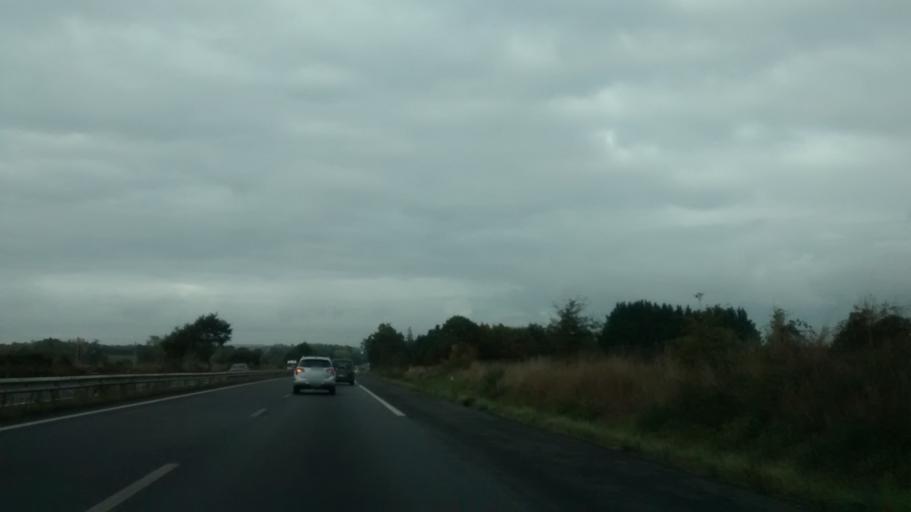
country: FR
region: Brittany
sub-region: Departement d'Ille-et-Vilaine
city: Saint-Didier
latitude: 48.0906
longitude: -1.3795
